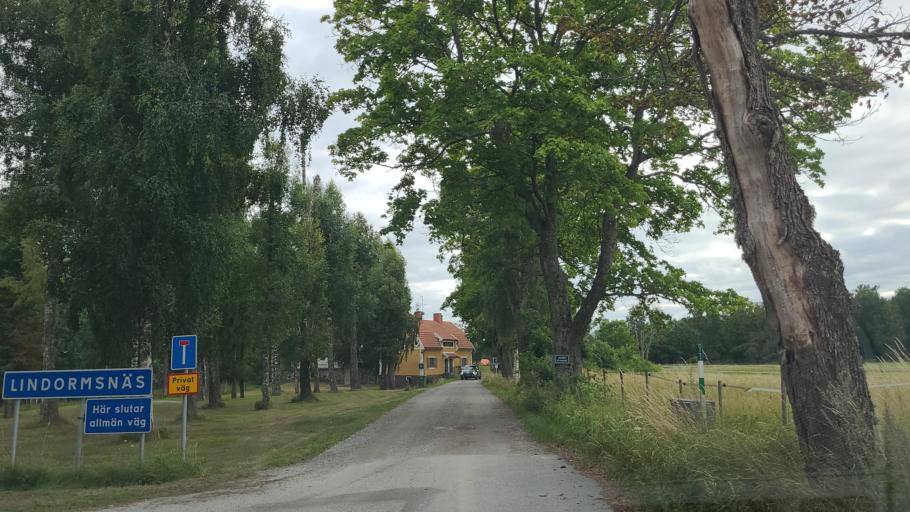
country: SE
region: Stockholm
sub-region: Upplands-Bro Kommun
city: Bro
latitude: 59.4865
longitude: 17.5659
